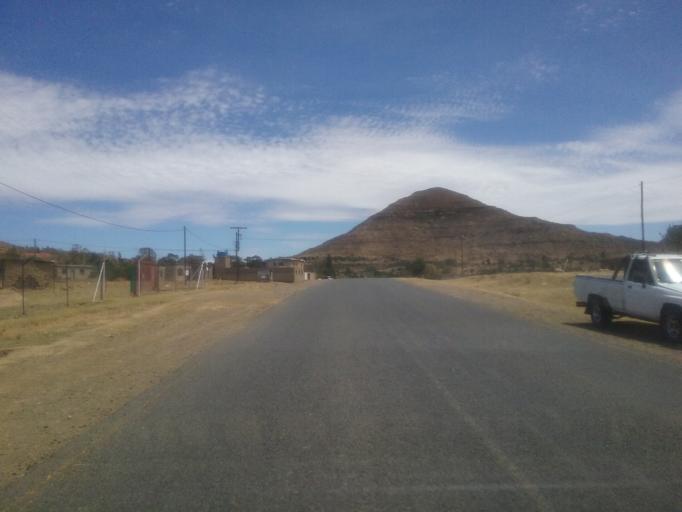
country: LS
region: Mafeteng
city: Mafeteng
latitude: -29.9577
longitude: 27.2895
